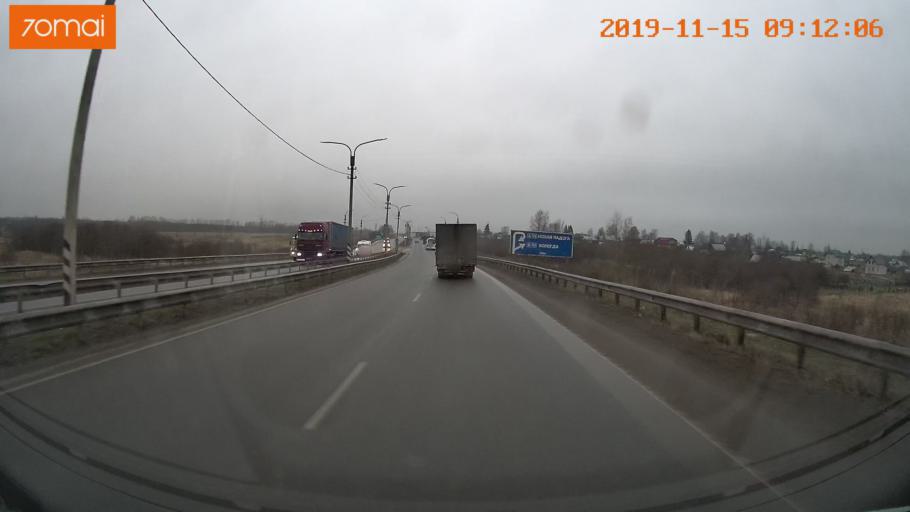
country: RU
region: Vologda
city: Tonshalovo
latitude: 59.2046
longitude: 37.9409
